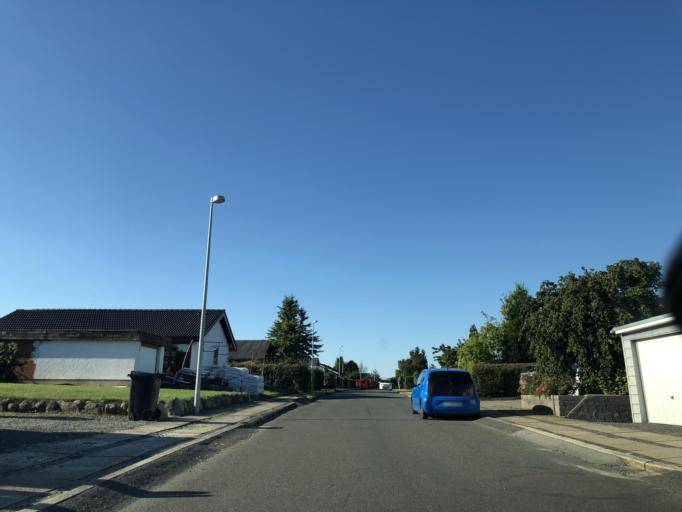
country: DK
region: North Denmark
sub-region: Mariagerfjord Kommune
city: Hobro
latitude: 56.6291
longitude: 9.8050
